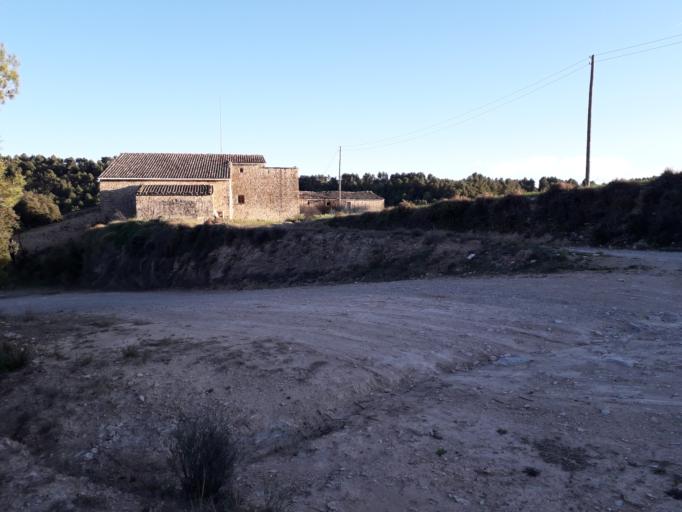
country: ES
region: Catalonia
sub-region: Provincia de Barcelona
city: Sant Marti de Tous
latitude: 41.5590
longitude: 1.4805
